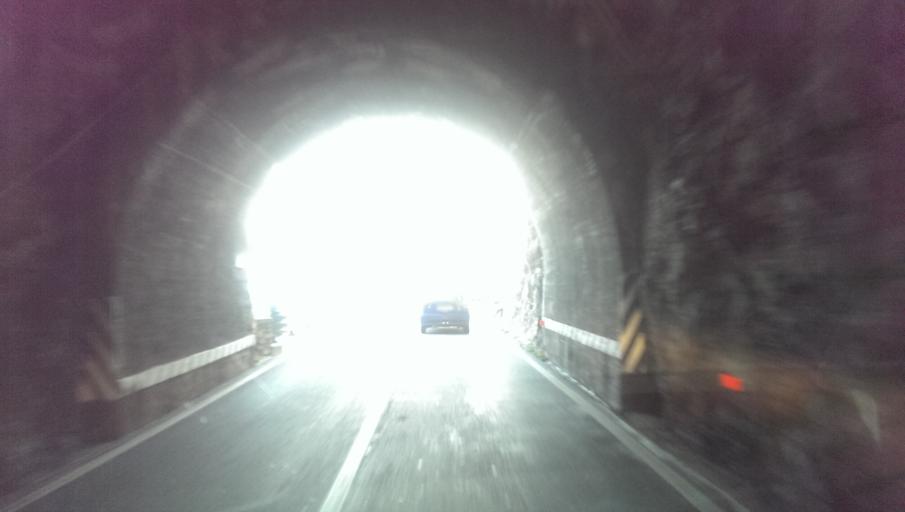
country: IT
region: Lombardy
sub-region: Provincia di Brescia
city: Limone sul Garda
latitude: 45.8326
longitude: 10.8249
